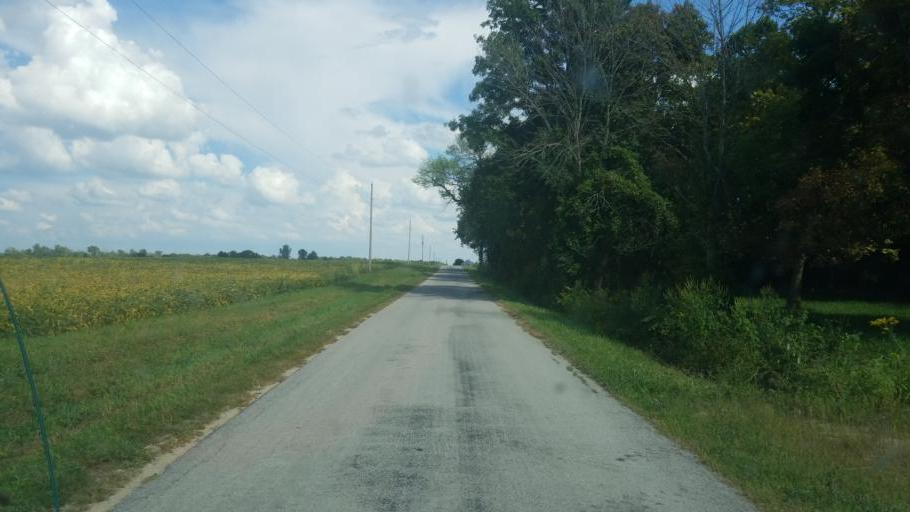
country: US
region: Ohio
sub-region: Seneca County
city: Tiffin
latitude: 40.9788
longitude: -83.1575
